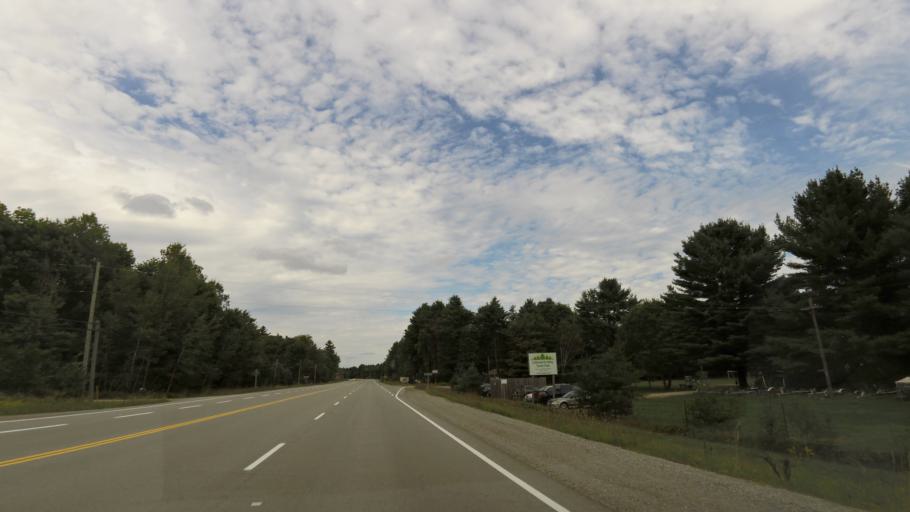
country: CA
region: Ontario
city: Omemee
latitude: 44.7801
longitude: -78.8106
